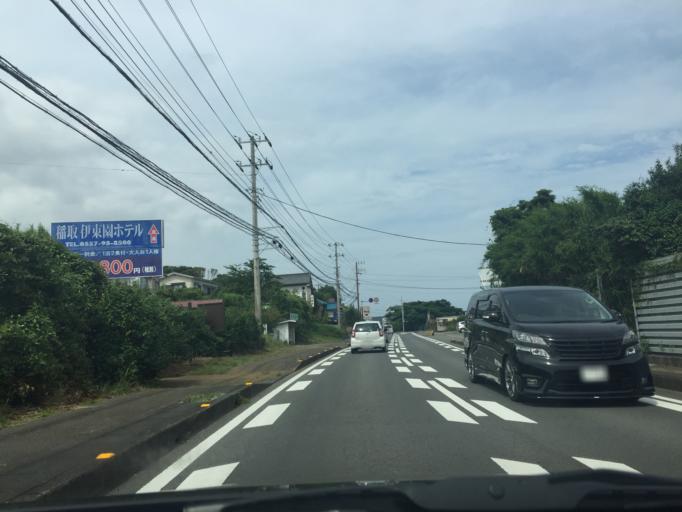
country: JP
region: Shizuoka
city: Shimoda
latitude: 34.7625
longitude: 139.0210
